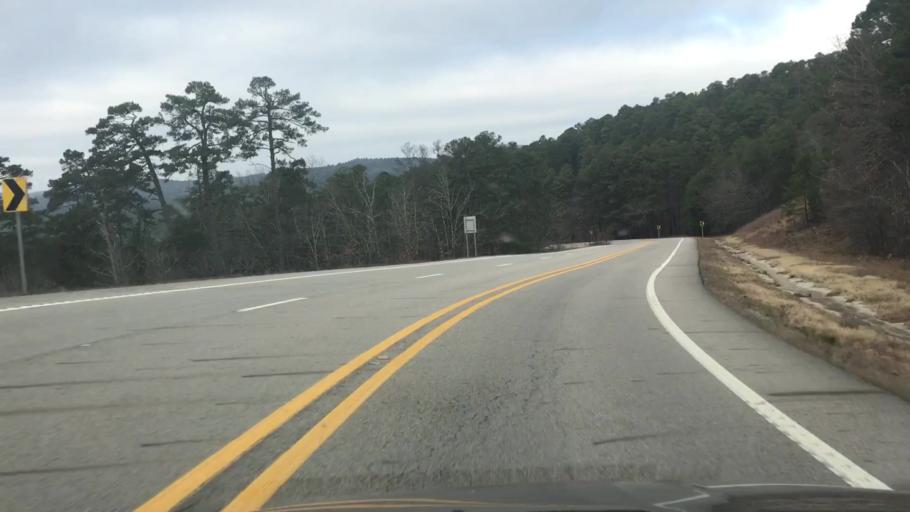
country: US
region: Arkansas
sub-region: Montgomery County
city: Mount Ida
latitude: 34.6820
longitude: -93.7972
